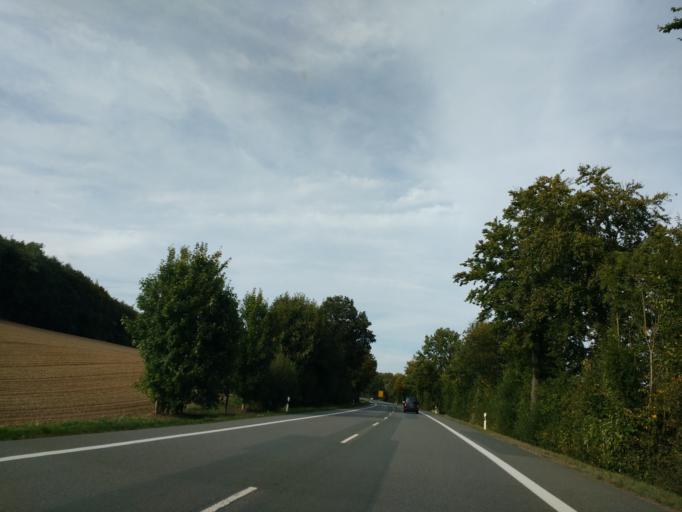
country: DE
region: North Rhine-Westphalia
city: Brakel
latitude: 51.7501
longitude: 9.1770
